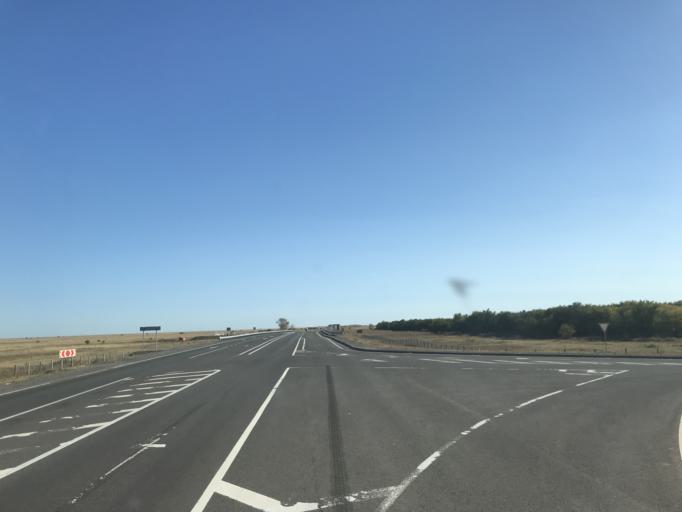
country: KZ
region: Pavlodar
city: Aksu
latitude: 52.0180
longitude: 77.2331
